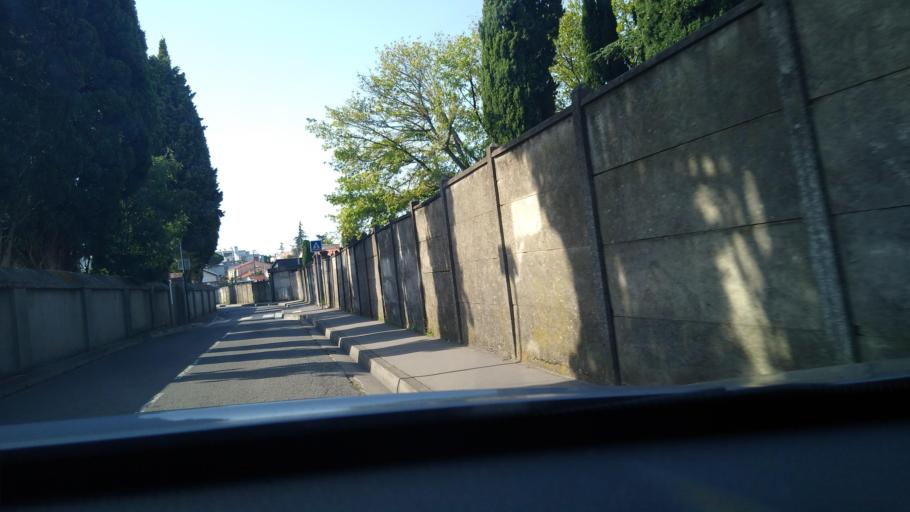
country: FR
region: Midi-Pyrenees
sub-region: Departement de la Haute-Garonne
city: Toulouse
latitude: 43.6093
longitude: 1.4658
